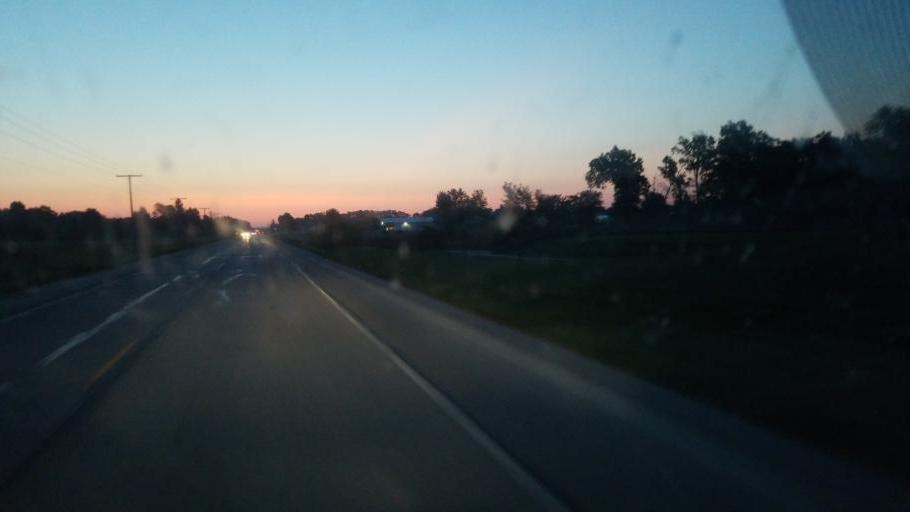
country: US
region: Indiana
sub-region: Elkhart County
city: Middlebury
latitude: 41.6761
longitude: -85.6094
